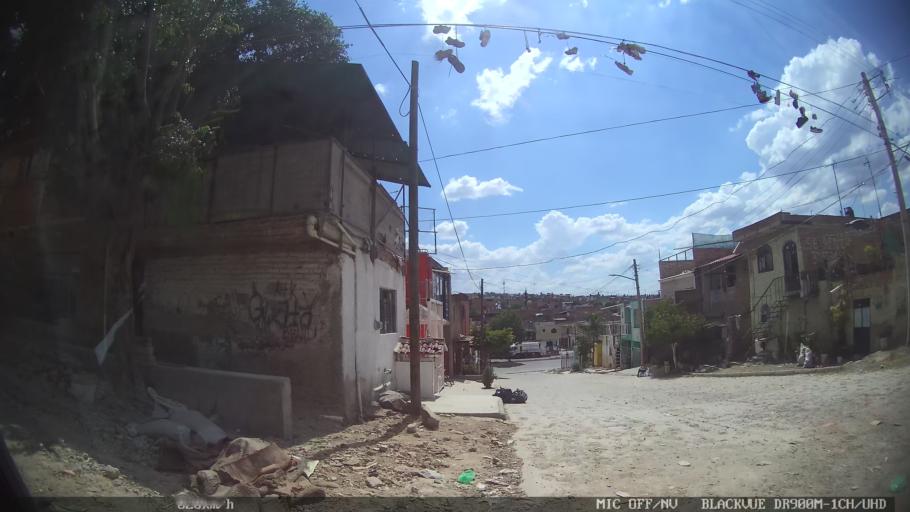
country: MX
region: Jalisco
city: Tlaquepaque
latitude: 20.6858
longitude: -103.2677
